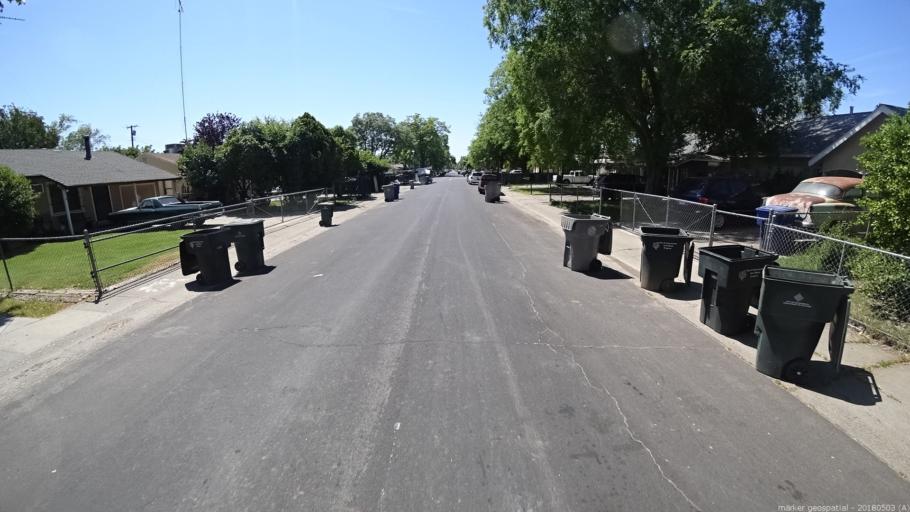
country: US
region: California
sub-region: Sacramento County
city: Rio Linda
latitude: 38.6391
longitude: -121.4278
